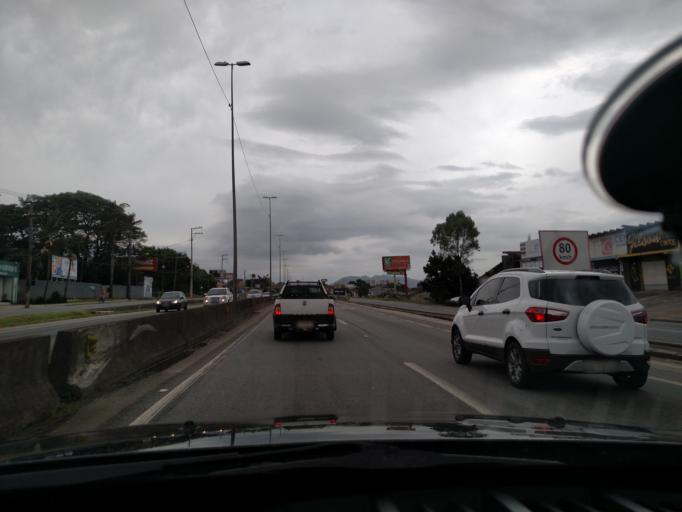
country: BR
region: Santa Catarina
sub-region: Sao Jose
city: Campinas
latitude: -27.5616
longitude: -48.6164
